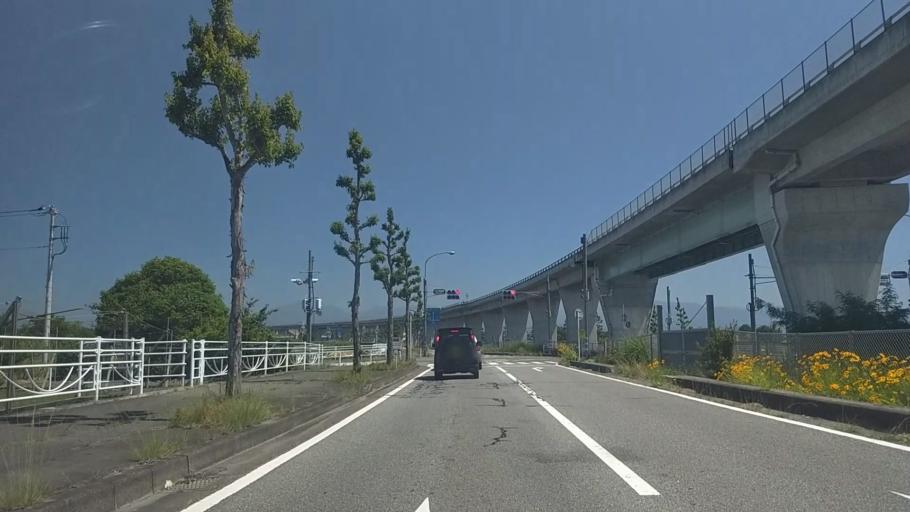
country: JP
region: Yamanashi
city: Ryuo
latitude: 35.6044
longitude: 138.4806
